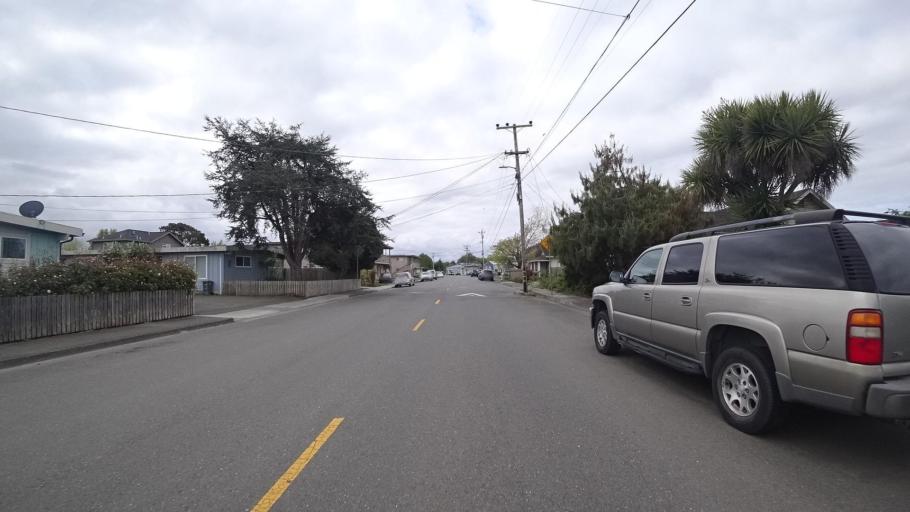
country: US
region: California
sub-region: Humboldt County
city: Arcata
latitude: 40.8640
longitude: -124.0887
